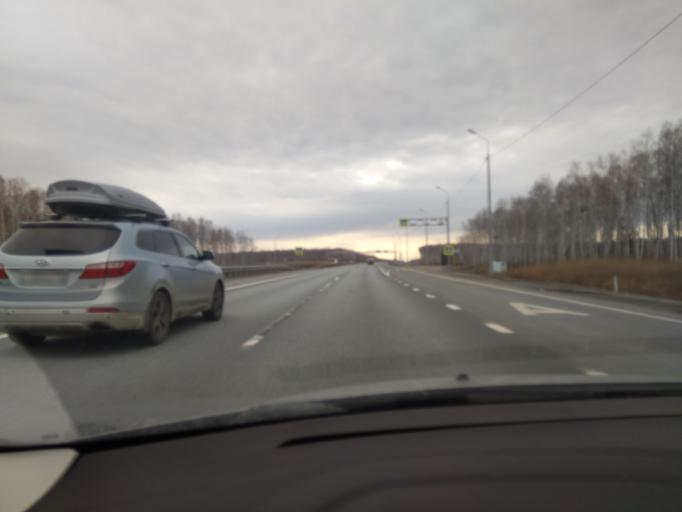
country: RU
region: Chelyabinsk
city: Chebarkul'
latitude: 54.9103
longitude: 60.4268
